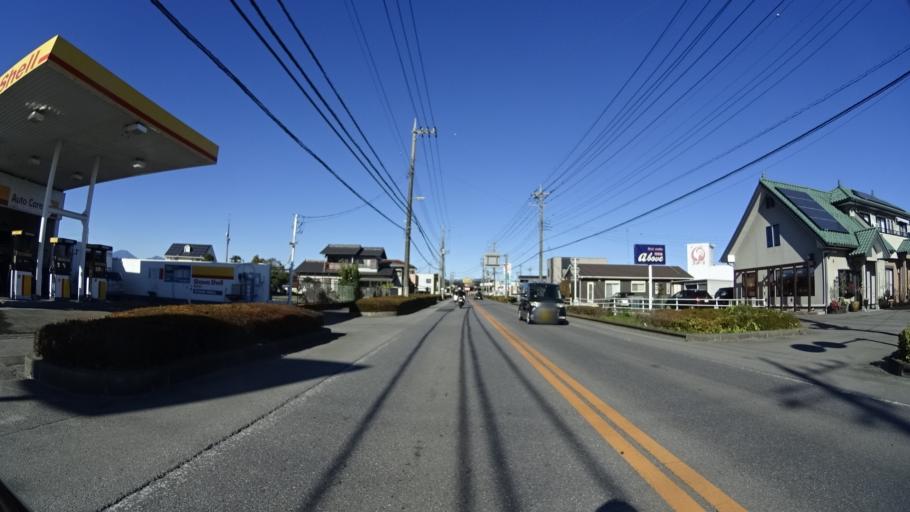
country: JP
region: Tochigi
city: Kanuma
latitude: 36.5148
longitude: 139.7517
